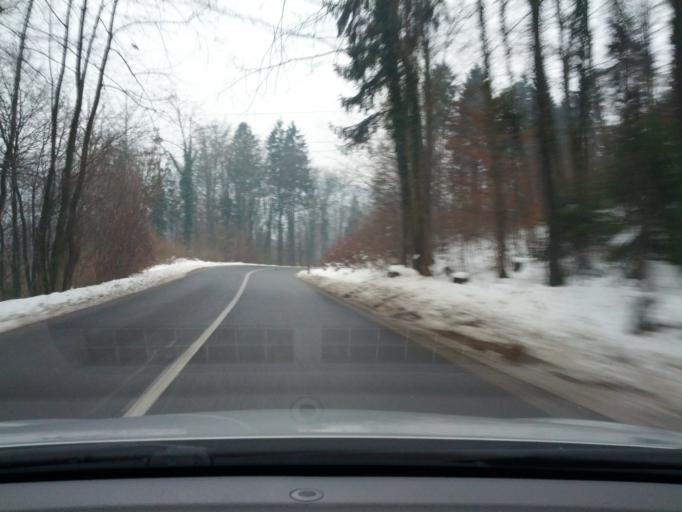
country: SI
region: Lukovica
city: Lukovica pri Domzalah
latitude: 46.1375
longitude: 14.7026
